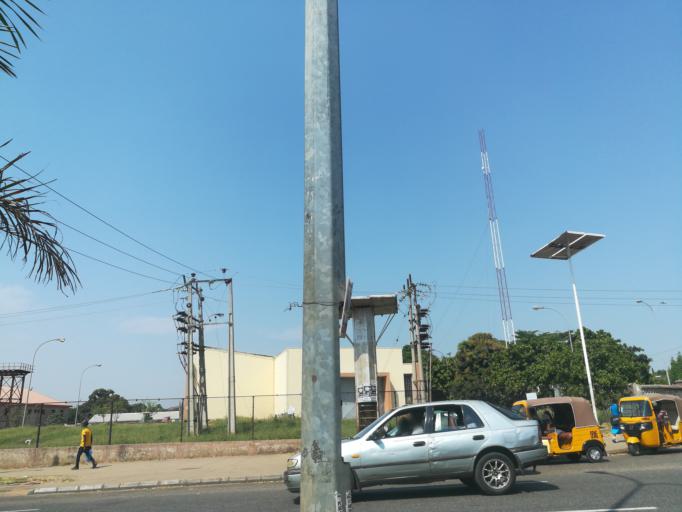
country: NG
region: Abuja Federal Capital Territory
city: Abuja
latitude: 9.0680
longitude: 7.4460
